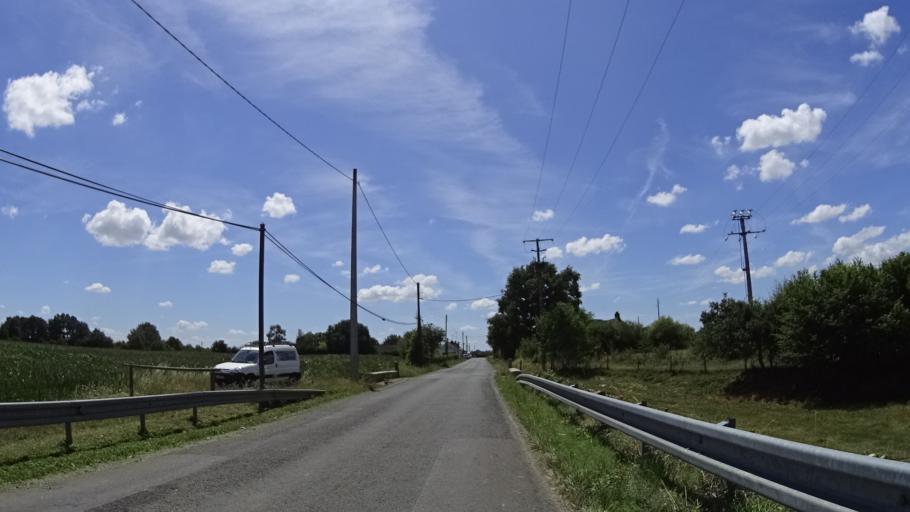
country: FR
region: Pays de la Loire
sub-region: Departement de Maine-et-Loire
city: Segre
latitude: 47.6126
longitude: -0.8969
